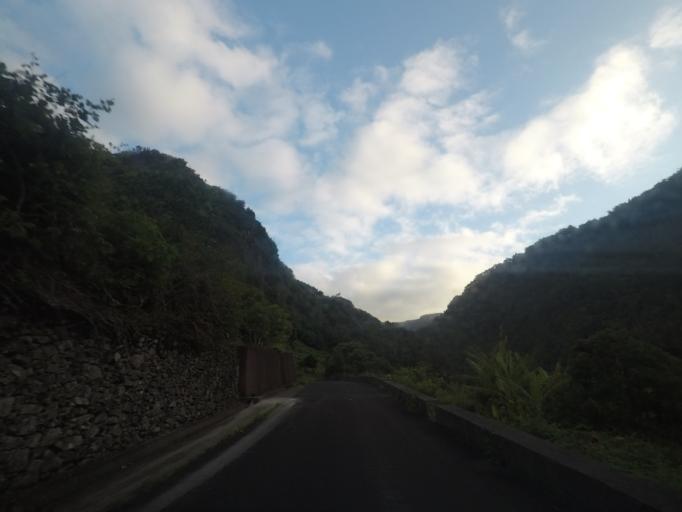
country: PT
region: Madeira
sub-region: Porto Moniz
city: Porto Moniz
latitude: 32.8486
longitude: -17.1612
